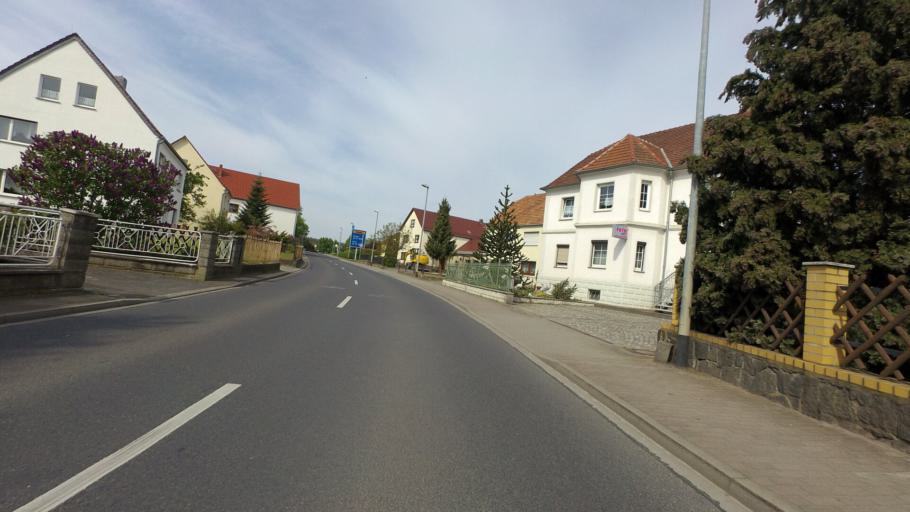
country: DE
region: Saxony
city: Thiendorf
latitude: 51.2950
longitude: 13.7388
